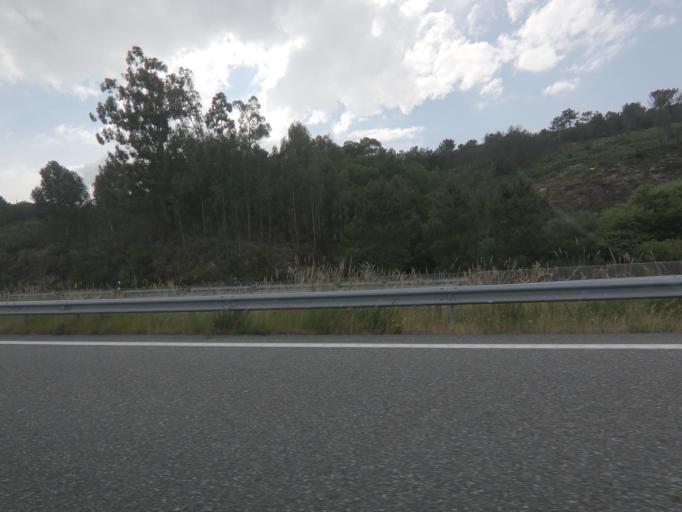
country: ES
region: Galicia
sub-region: Provincia de Ourense
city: Melon
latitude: 42.2451
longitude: -8.2266
